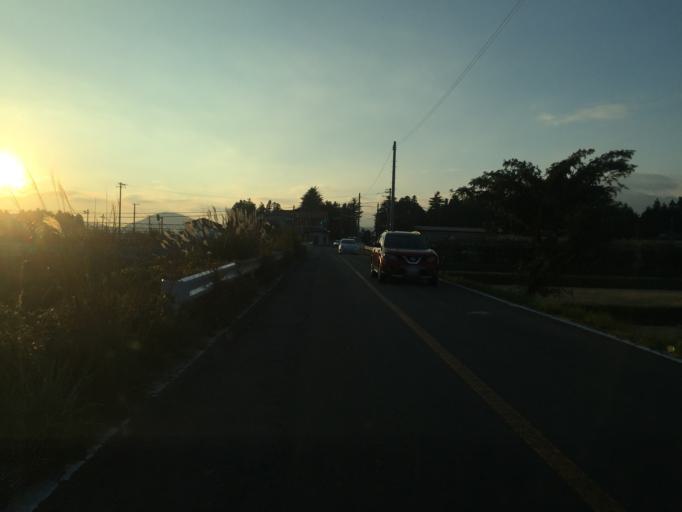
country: JP
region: Fukushima
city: Motomiya
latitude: 37.5426
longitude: 140.3793
